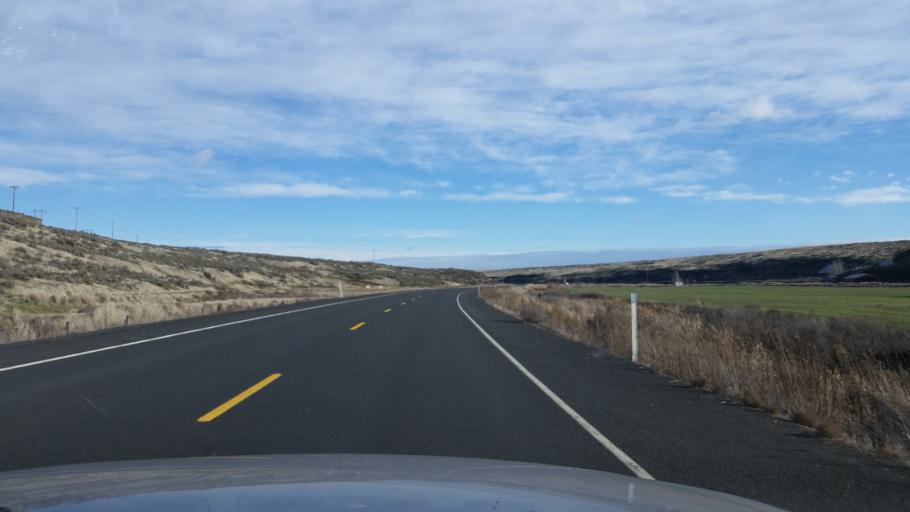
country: US
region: Washington
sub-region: Adams County
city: Ritzville
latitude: 47.3583
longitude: -118.5101
